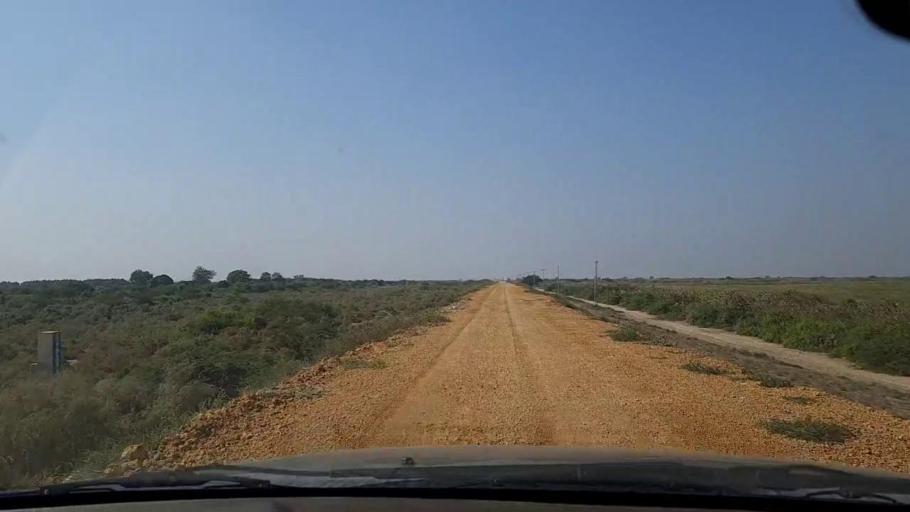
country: PK
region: Sindh
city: Chuhar Jamali
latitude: 24.4614
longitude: 67.8996
